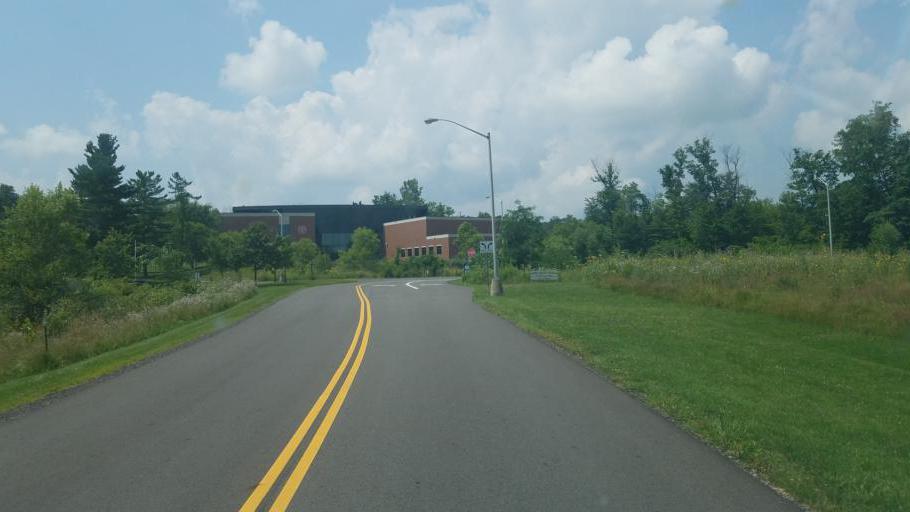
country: US
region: Ohio
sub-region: Richland County
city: Ontario
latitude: 40.8007
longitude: -82.5744
